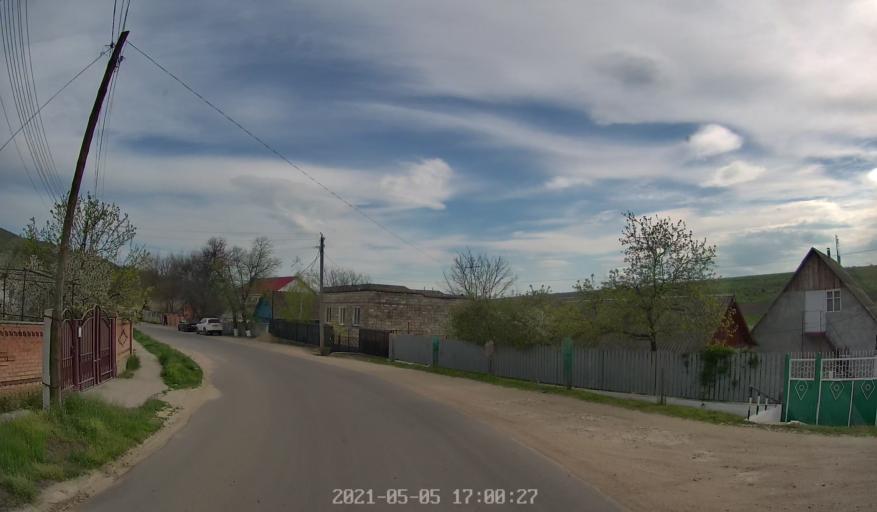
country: MD
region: Chisinau
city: Vadul lui Voda
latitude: 47.0642
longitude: 29.1308
